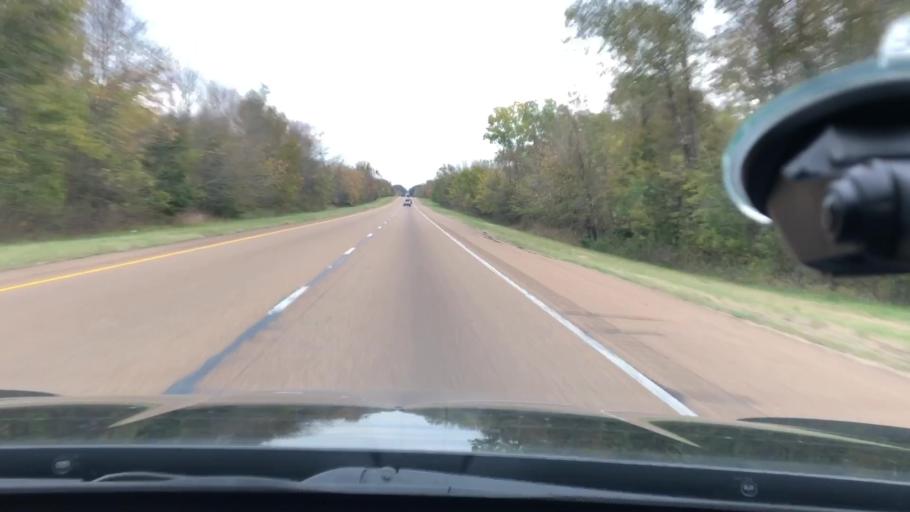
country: US
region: Arkansas
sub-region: Hempstead County
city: Hope
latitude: 33.7506
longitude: -93.5051
